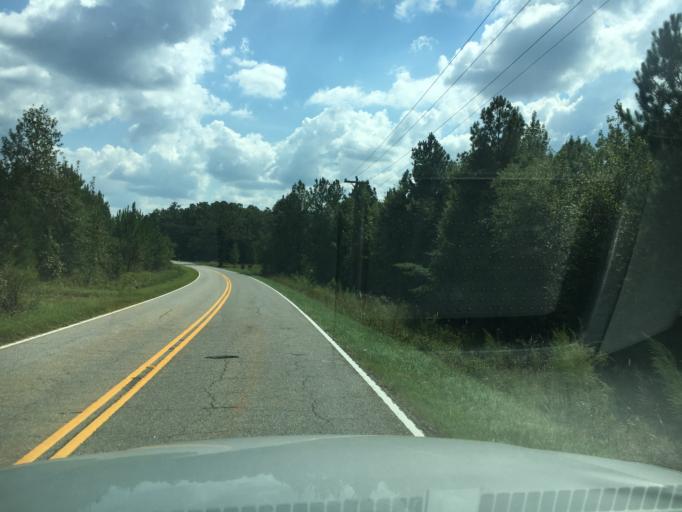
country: US
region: South Carolina
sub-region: Greenwood County
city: Greenwood
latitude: 34.0663
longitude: -82.1464
